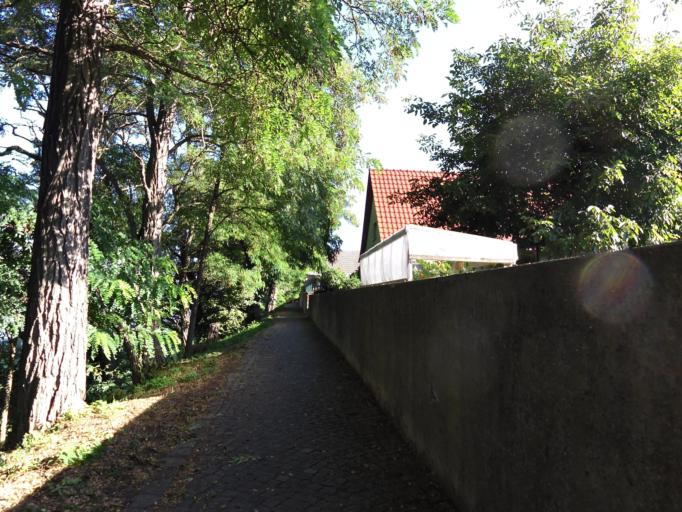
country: DE
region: Saxony
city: Nunchritz
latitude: 51.2673
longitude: 13.4051
